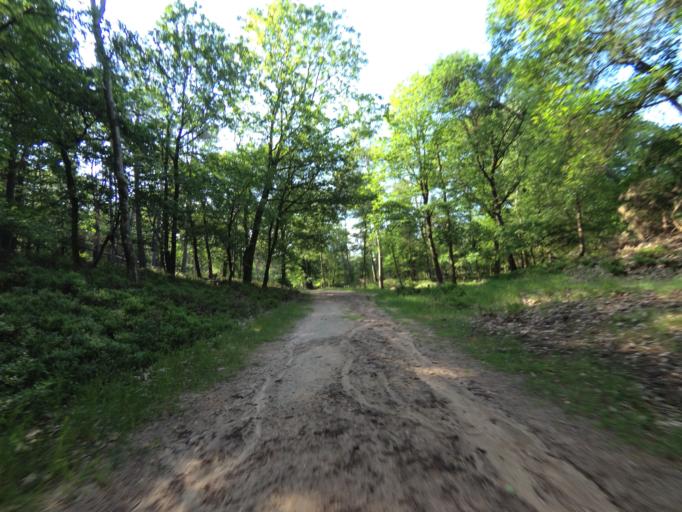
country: NL
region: Gelderland
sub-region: Gemeente Apeldoorn
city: Beekbergen
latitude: 52.1551
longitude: 5.9019
